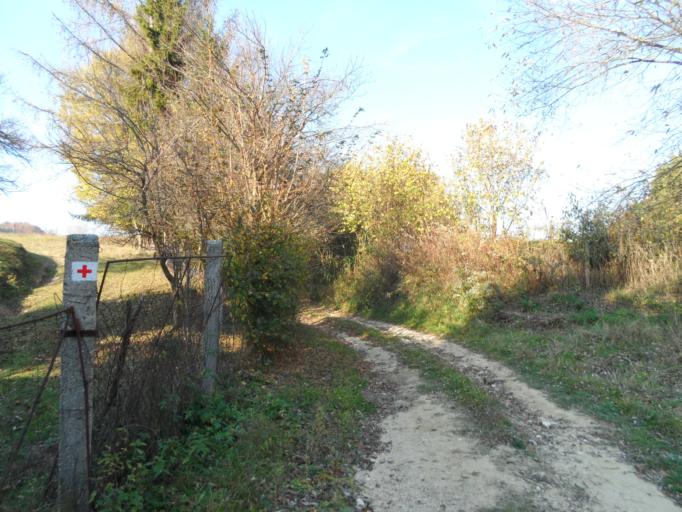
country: HU
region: Veszprem
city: Herend
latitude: 47.1828
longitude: 17.6823
